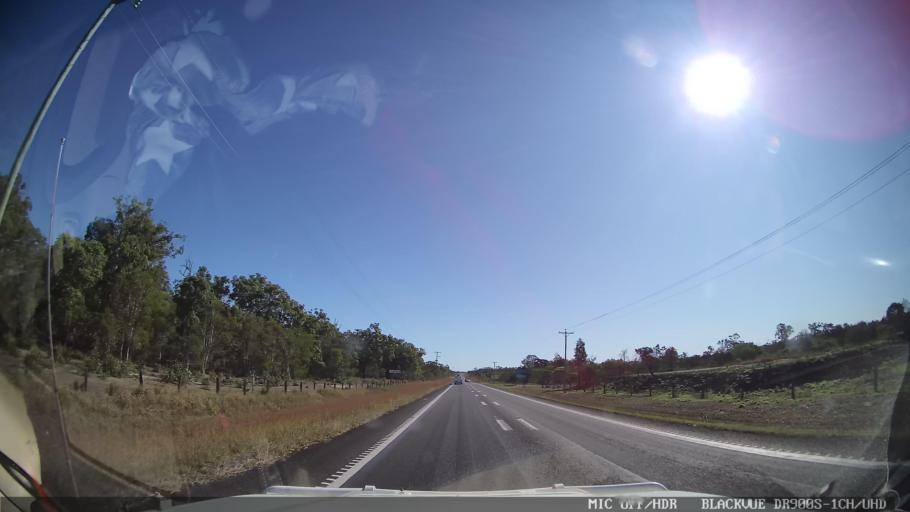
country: AU
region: Queensland
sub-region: Bundaberg
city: Childers
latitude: -25.2503
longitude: 152.3483
